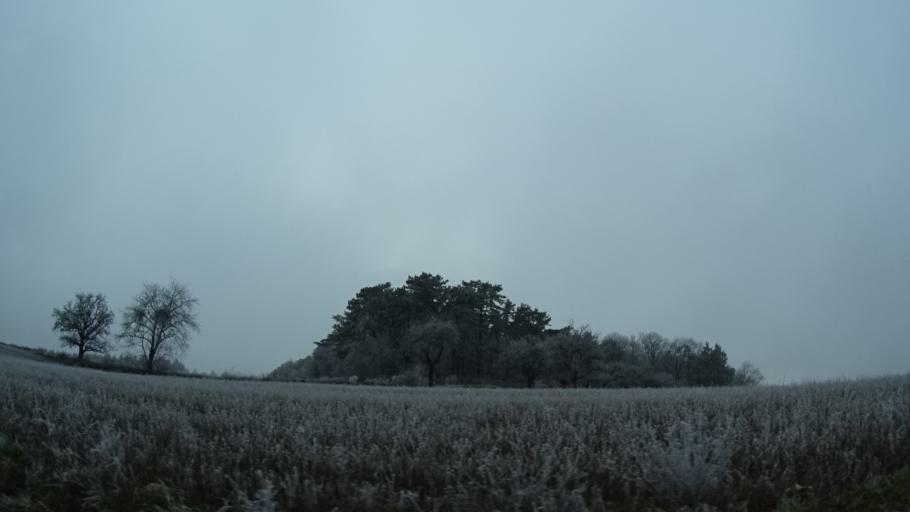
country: DE
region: Baden-Wuerttemberg
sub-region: Regierungsbezirk Stuttgart
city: Boxberg
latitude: 49.5016
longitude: 9.6331
